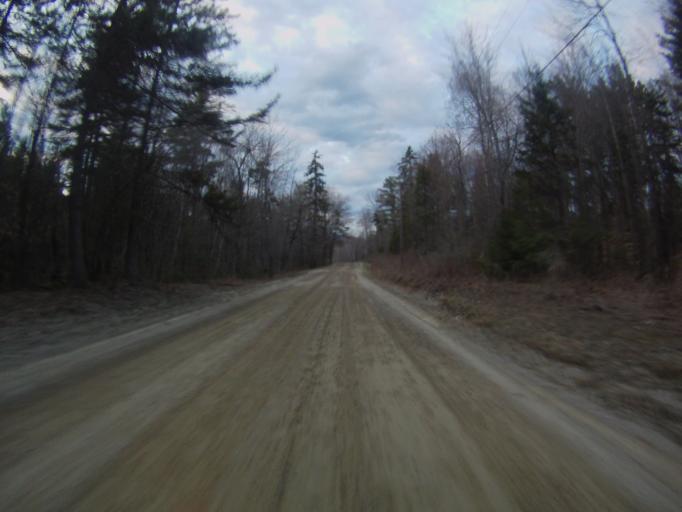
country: US
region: Vermont
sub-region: Addison County
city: Middlebury (village)
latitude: 43.9574
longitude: -73.0261
